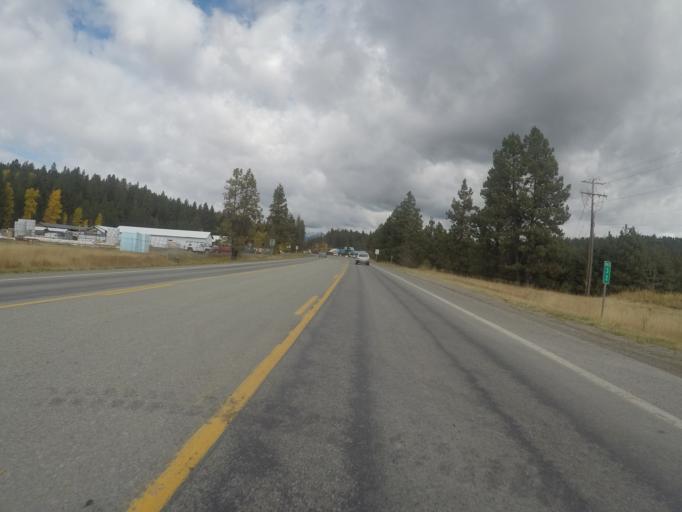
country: US
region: Montana
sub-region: Flathead County
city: Bigfork
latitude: 48.0747
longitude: -114.0788
